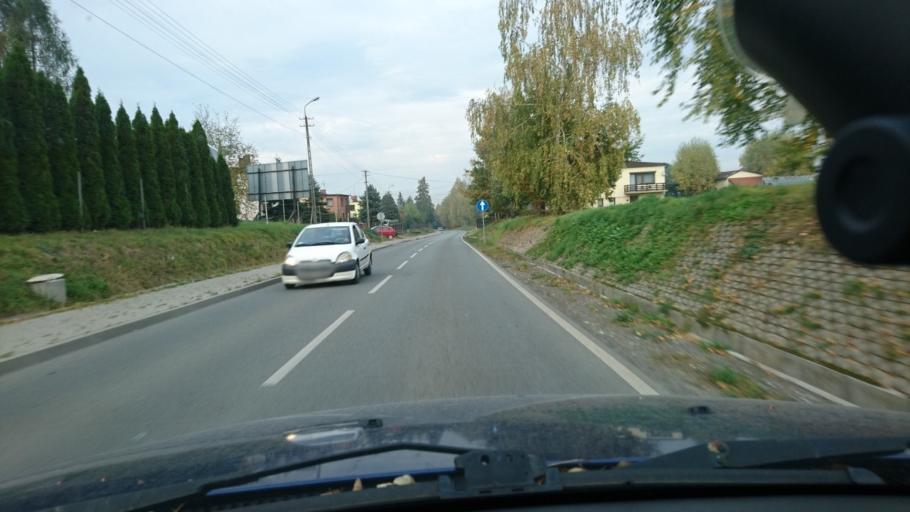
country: PL
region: Silesian Voivodeship
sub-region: Powiat bielski
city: Kozy
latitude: 49.8550
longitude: 19.1393
